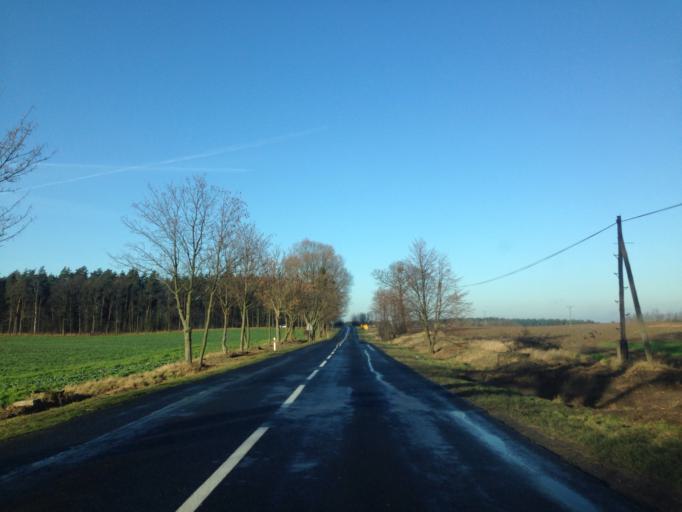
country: PL
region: Kujawsko-Pomorskie
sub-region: Powiat brodnicki
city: Bobrowo
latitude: 53.3194
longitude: 19.2723
